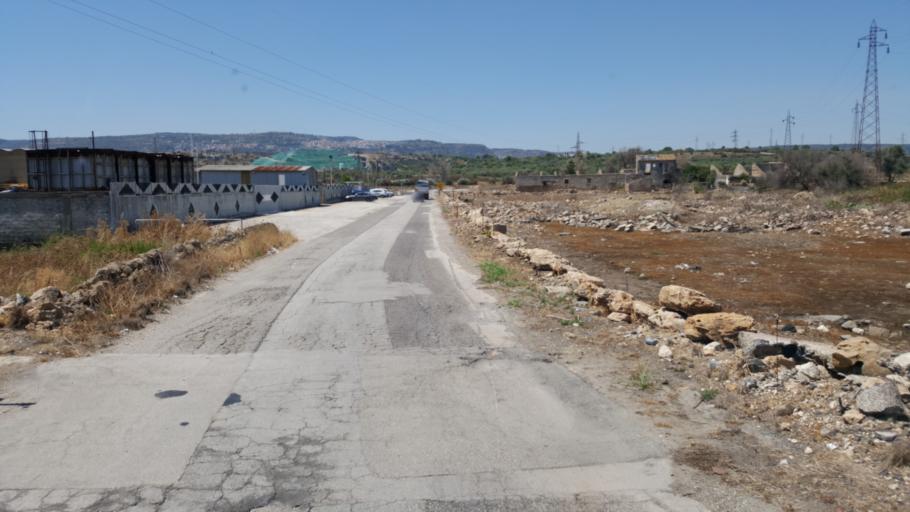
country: IT
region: Sicily
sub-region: Provincia di Siracusa
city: Melilli
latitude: 37.2044
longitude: 15.1636
